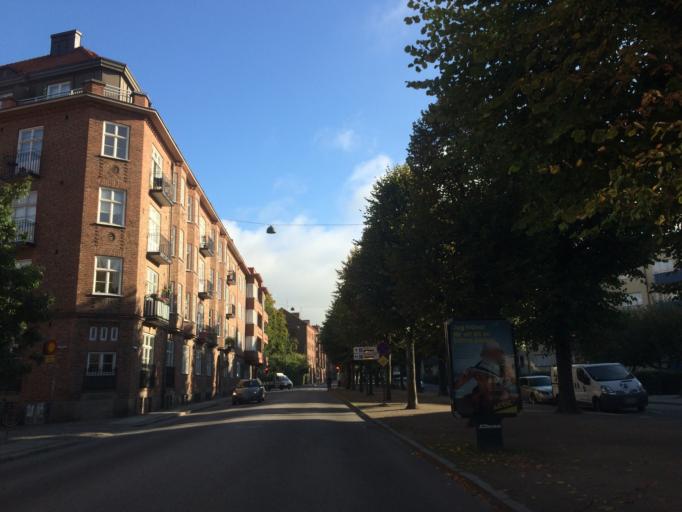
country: SE
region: Skane
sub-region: Lunds Kommun
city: Lund
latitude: 55.6978
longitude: 13.1951
